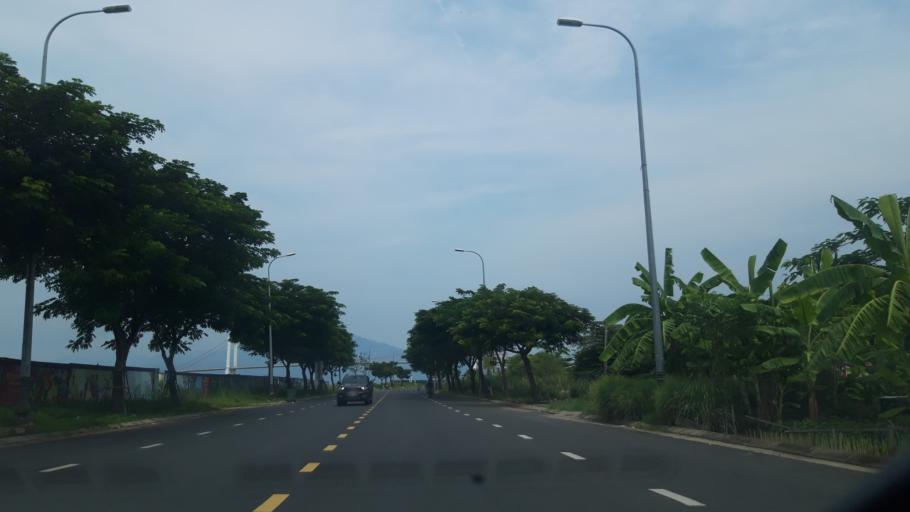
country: VN
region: Da Nang
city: Da Nang
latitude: 16.0887
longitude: 108.2286
